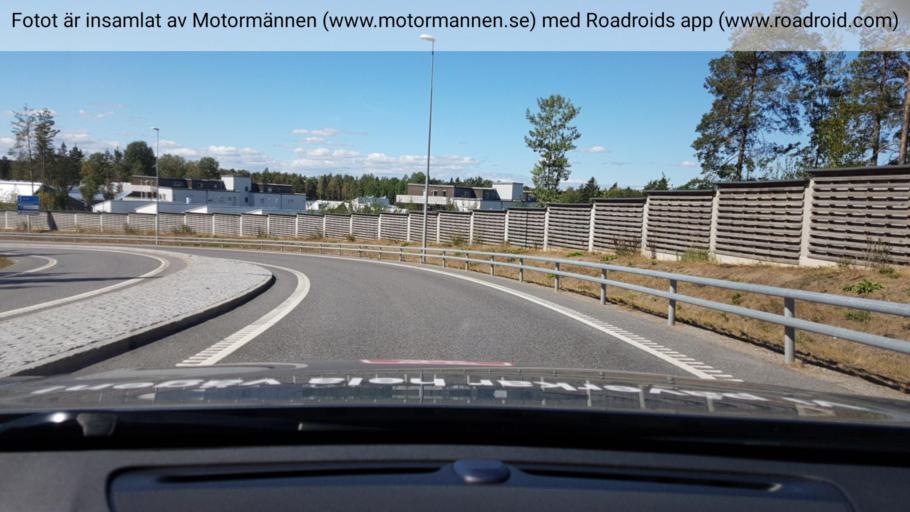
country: SE
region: Stockholm
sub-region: Nacka Kommun
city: Alta
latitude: 59.2492
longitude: 18.1934
